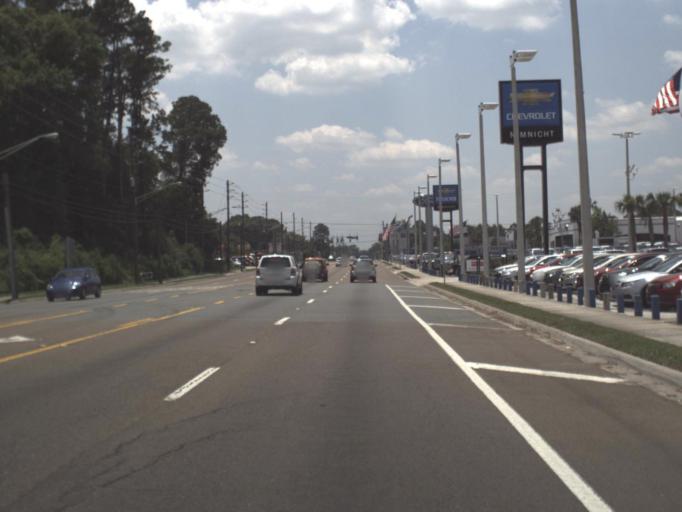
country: US
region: Florida
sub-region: Duval County
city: Jacksonville
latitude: 30.2914
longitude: -81.7305
